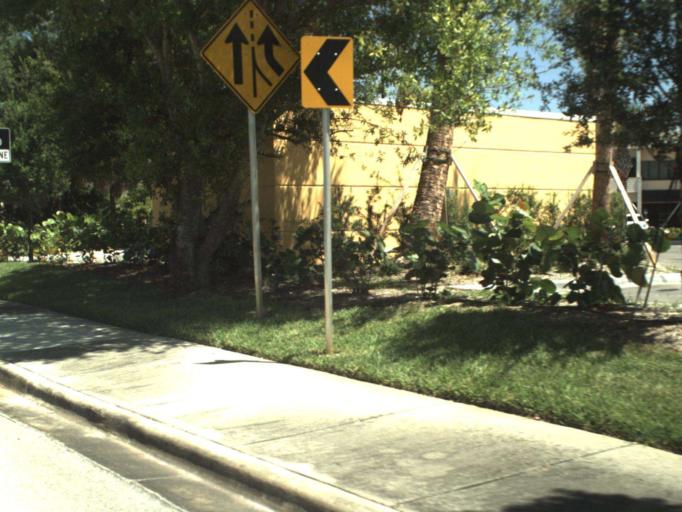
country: US
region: Florida
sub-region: Indian River County
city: Vero Beach
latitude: 27.6384
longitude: -80.3865
